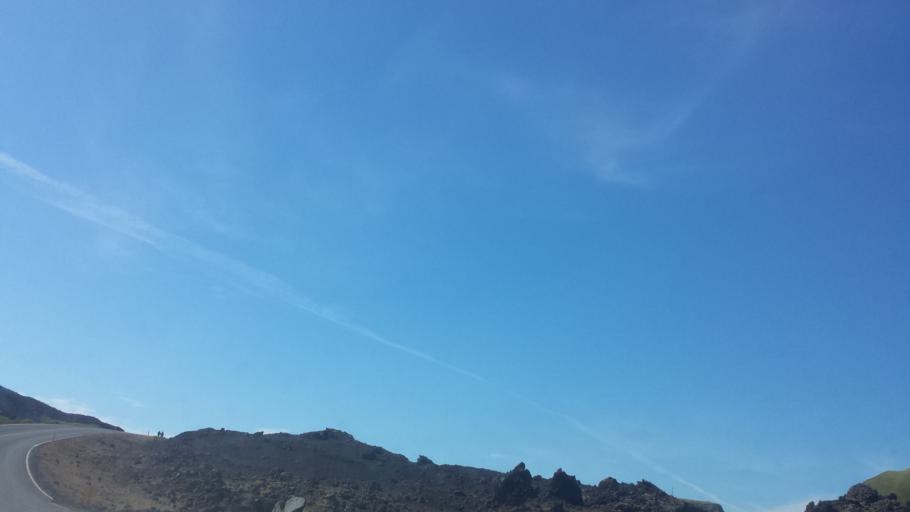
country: IS
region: South
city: Vestmannaeyjar
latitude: 63.4429
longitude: -20.2386
